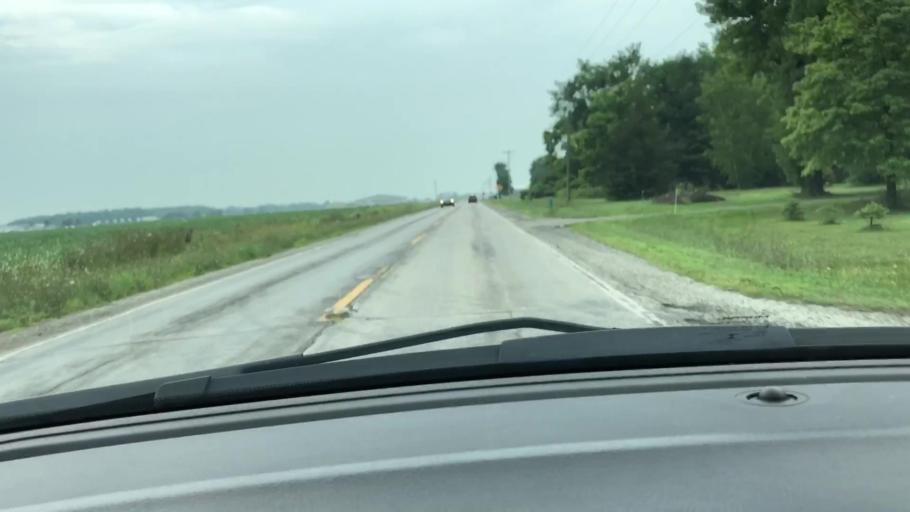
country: US
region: Michigan
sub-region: Saginaw County
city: Freeland
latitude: 43.5173
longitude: -84.0907
